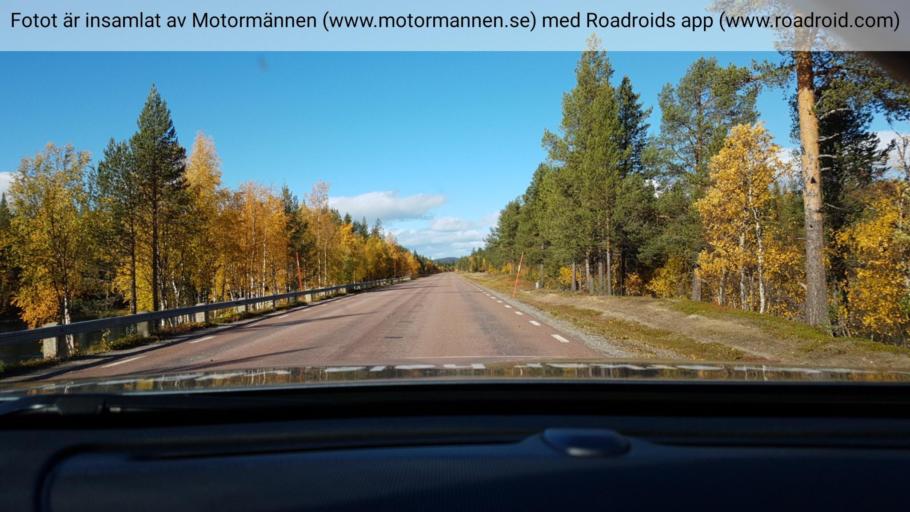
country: SE
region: Norrbotten
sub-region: Arjeplogs Kommun
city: Arjeplog
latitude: 66.0068
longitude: 18.1059
